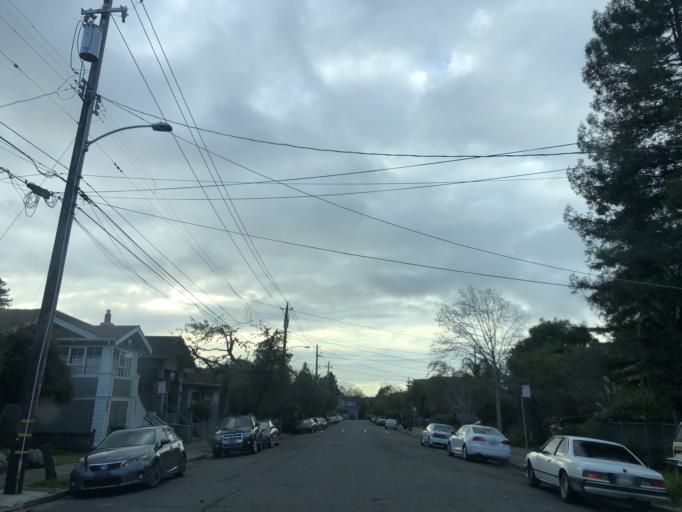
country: US
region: California
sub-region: Alameda County
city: Emeryville
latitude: 37.8426
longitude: -122.2654
